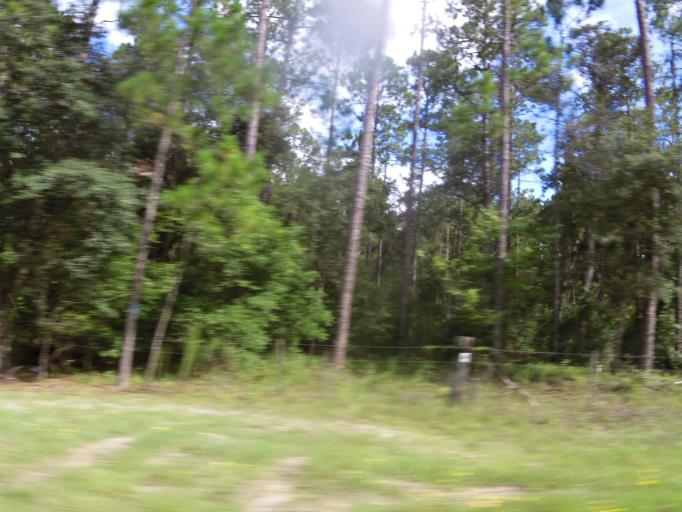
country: US
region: Florida
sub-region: Clay County
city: Green Cove Springs
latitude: 29.9351
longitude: -81.6673
